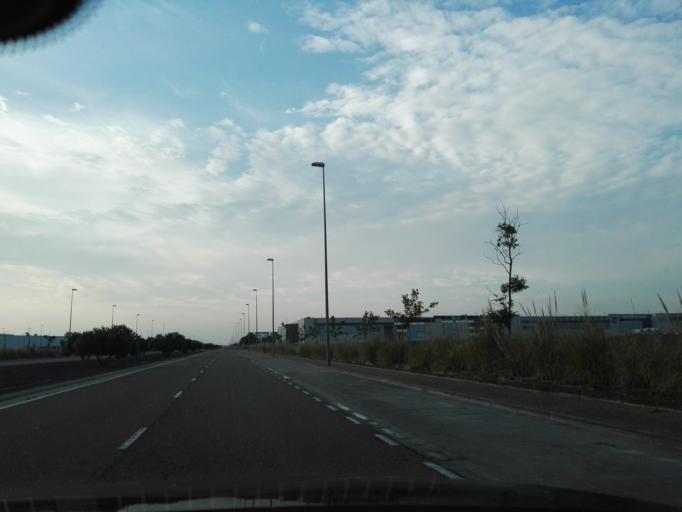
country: ES
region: Aragon
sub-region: Provincia de Zaragoza
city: Utebo
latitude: 41.6525
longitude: -0.9972
